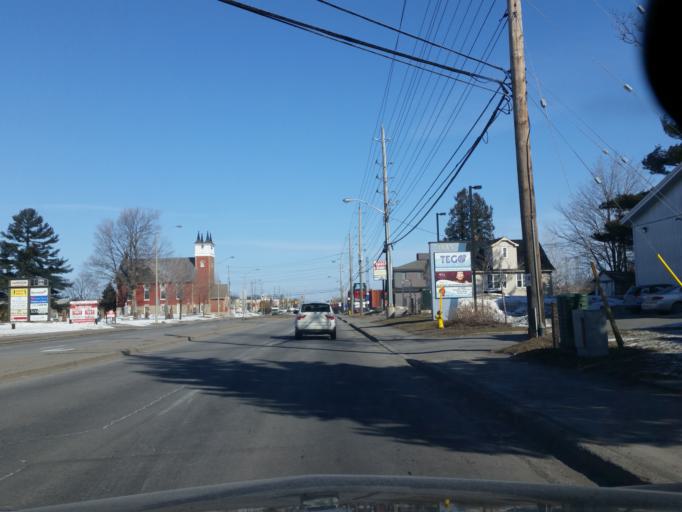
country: CA
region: Ontario
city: Ottawa
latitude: 45.3316
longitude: -75.7222
